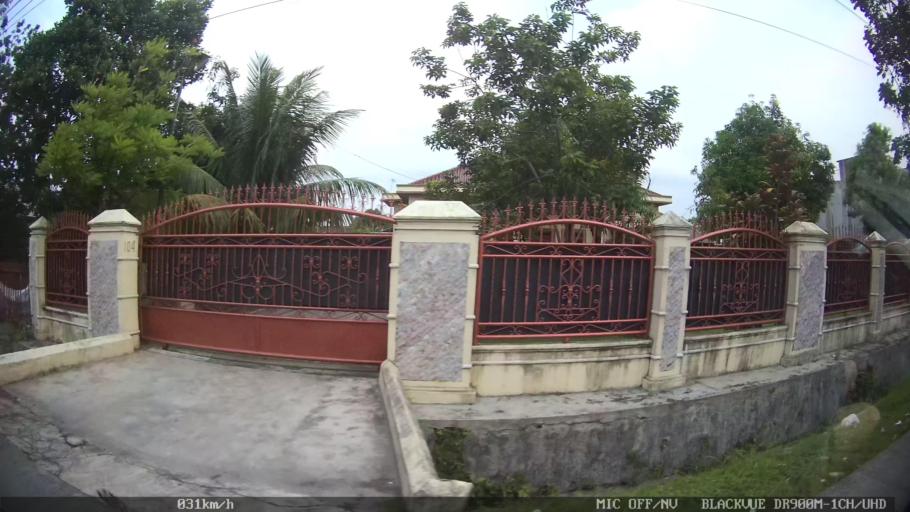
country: ID
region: North Sumatra
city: Medan
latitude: 3.6093
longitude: 98.7001
